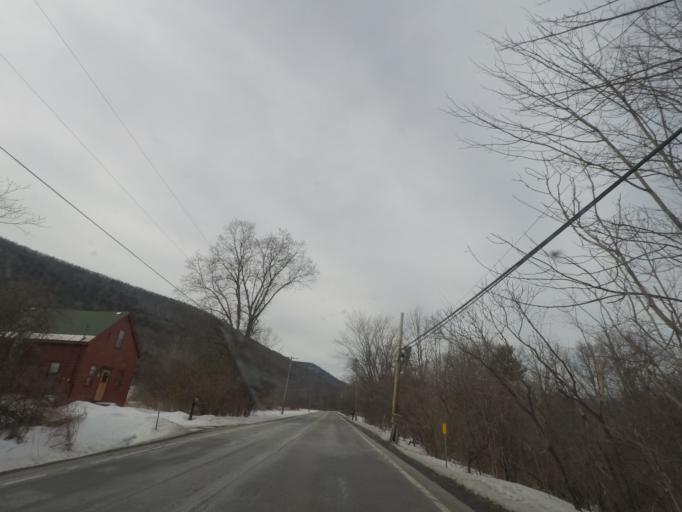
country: US
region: New York
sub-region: Albany County
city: Altamont
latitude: 42.6725
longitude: -74.0108
